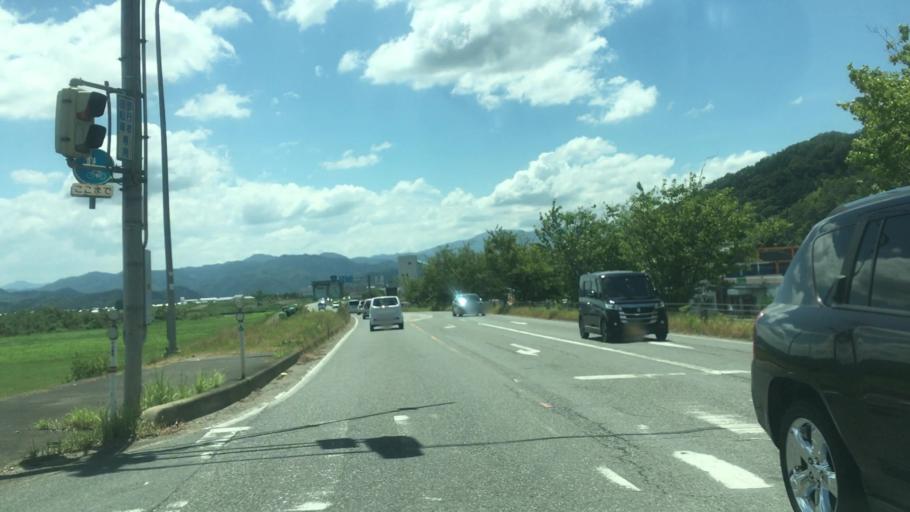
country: JP
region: Hyogo
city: Toyooka
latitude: 35.5068
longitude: 134.8149
